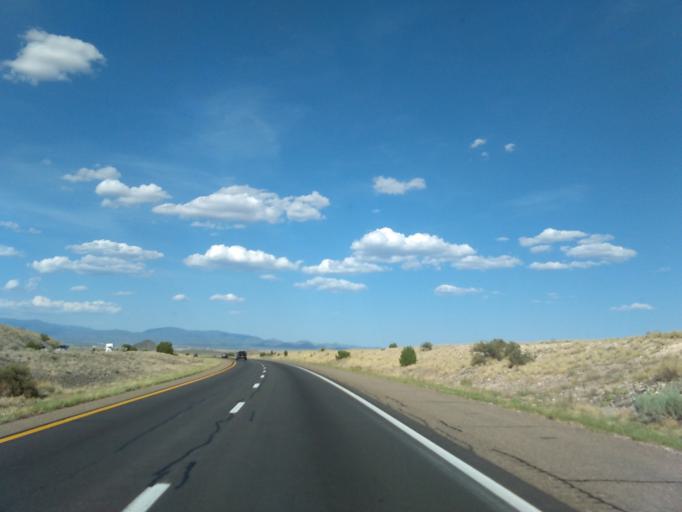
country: US
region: New Mexico
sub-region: Santa Fe County
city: La Cienega
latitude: 35.5211
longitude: -106.1683
